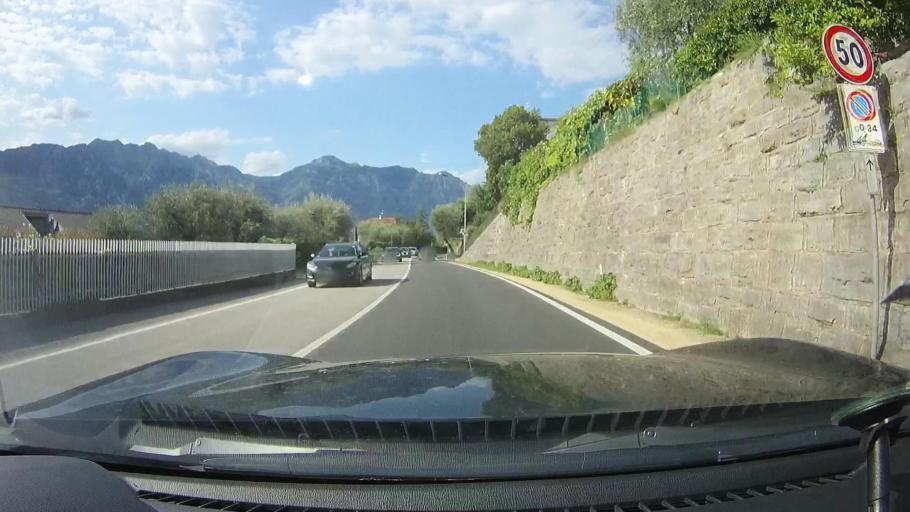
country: IT
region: Veneto
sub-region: Provincia di Verona
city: Malcesine
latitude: 45.7695
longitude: 10.8121
